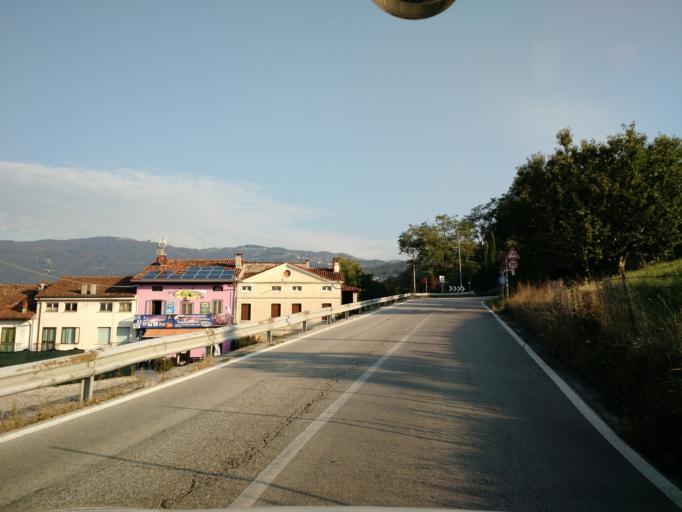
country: IT
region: Veneto
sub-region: Provincia di Vicenza
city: Salcedo
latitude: 45.7514
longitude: 11.5576
